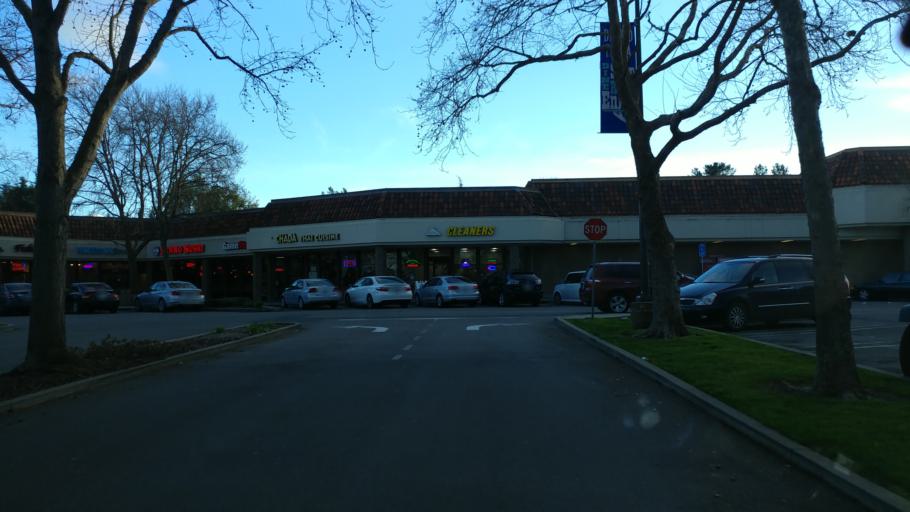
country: US
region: California
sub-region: Contra Costa County
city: San Ramon
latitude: 37.7742
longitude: -121.9772
